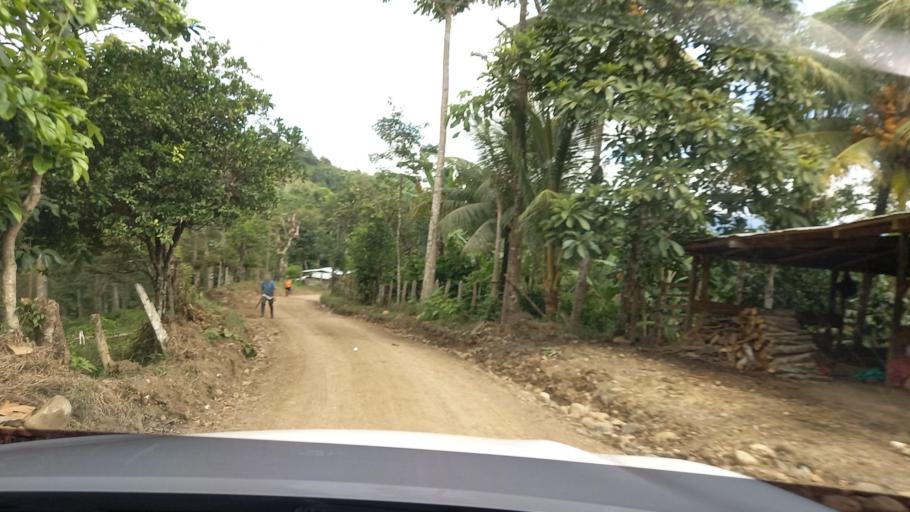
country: NI
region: Jinotega
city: San Jose de Bocay
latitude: 13.3758
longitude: -85.6841
